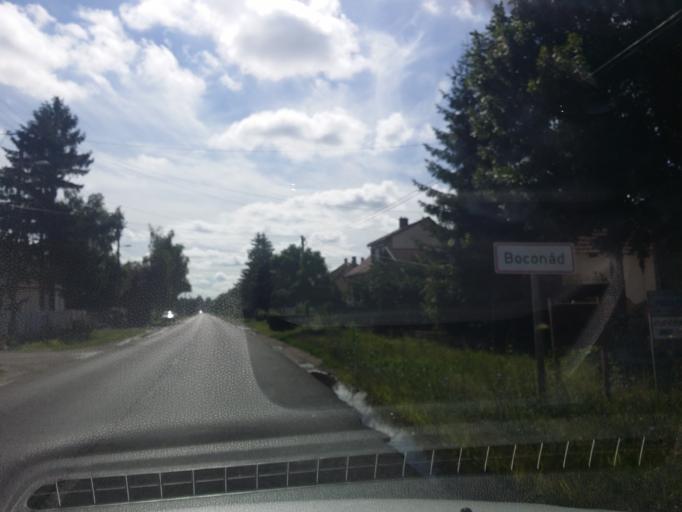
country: HU
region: Jasz-Nagykun-Szolnok
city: Jaszszentandras
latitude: 47.6434
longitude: 20.1786
